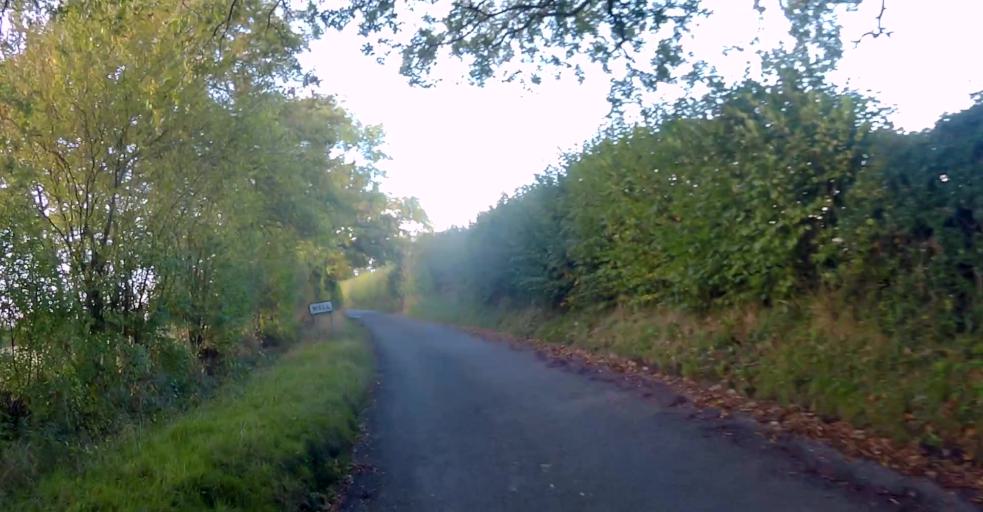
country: GB
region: England
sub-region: Hampshire
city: Long Sutton
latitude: 51.2109
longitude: -0.9063
